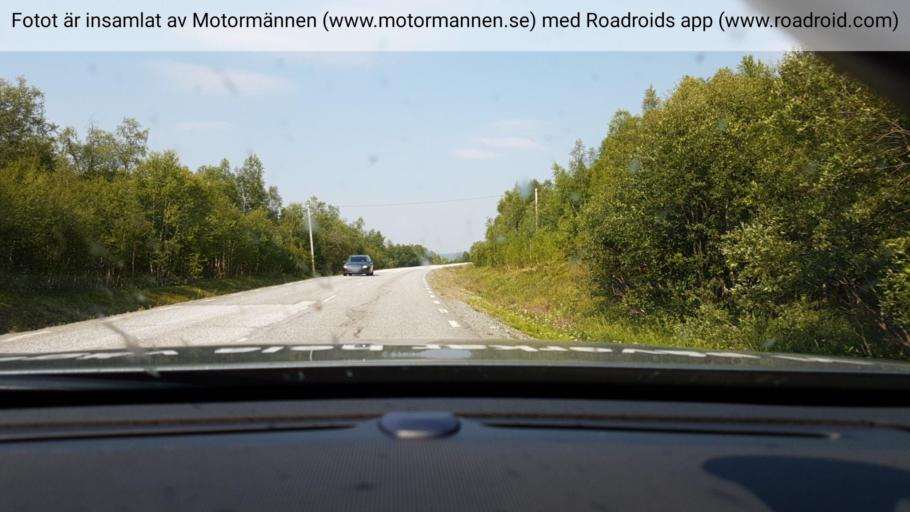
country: NO
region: Nordland
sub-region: Rana
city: Mo i Rana
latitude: 65.7815
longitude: 15.1214
